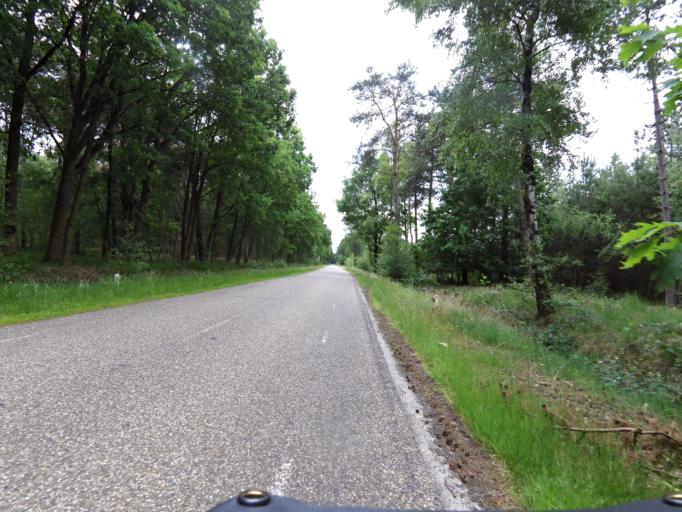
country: NL
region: North Brabant
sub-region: Gemeente Oirschot
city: Middelbeers
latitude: 51.4279
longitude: 5.2141
